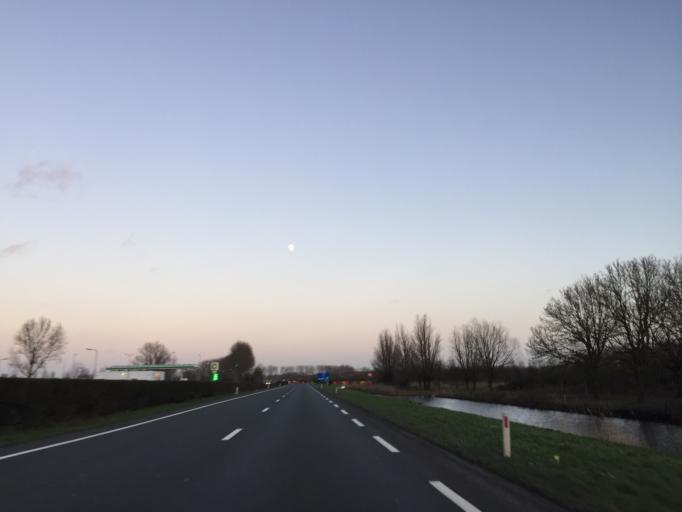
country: NL
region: South Holland
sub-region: Gemeente Lansingerland
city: Berkel en Rodenrijs
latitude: 51.9706
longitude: 4.4723
